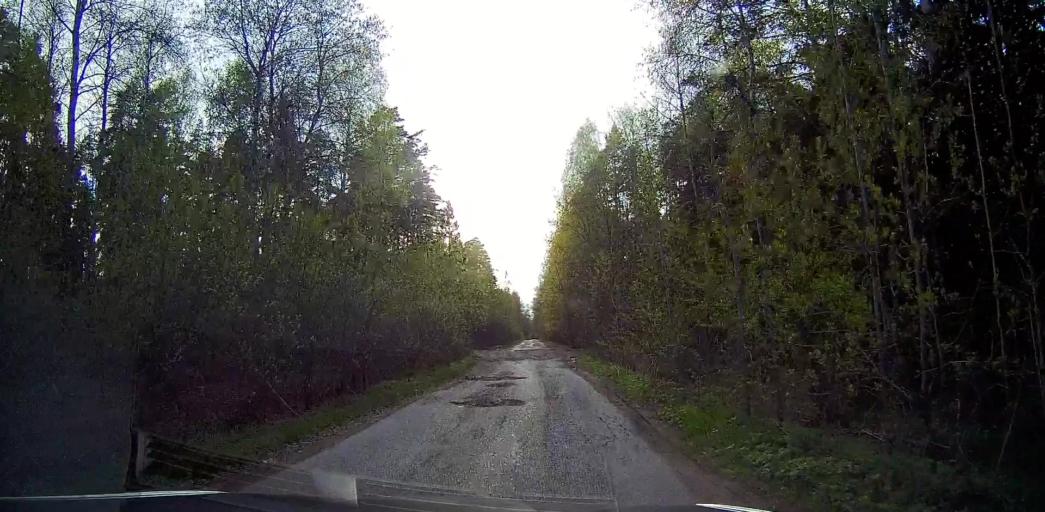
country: RU
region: Moskovskaya
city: Malyshevo
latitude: 55.5516
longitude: 38.3498
